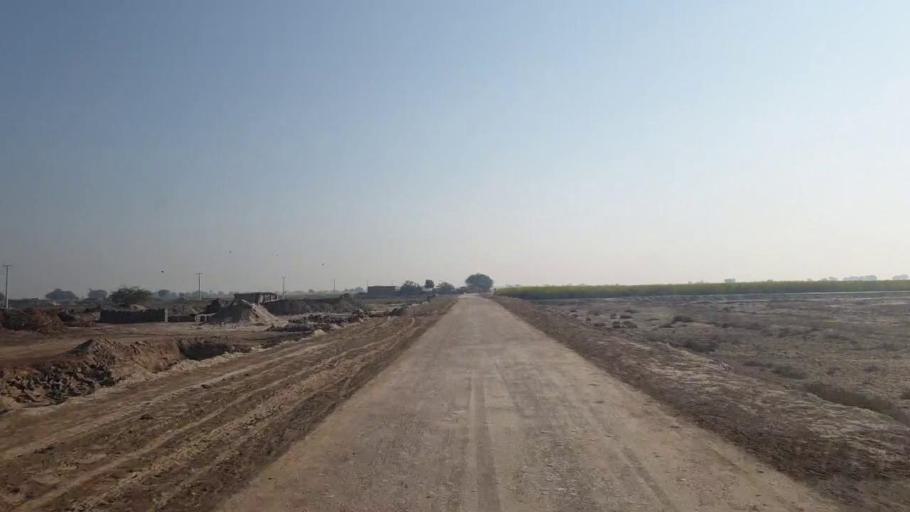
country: PK
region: Sindh
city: Shahpur Chakar
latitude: 26.0658
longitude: 68.5943
